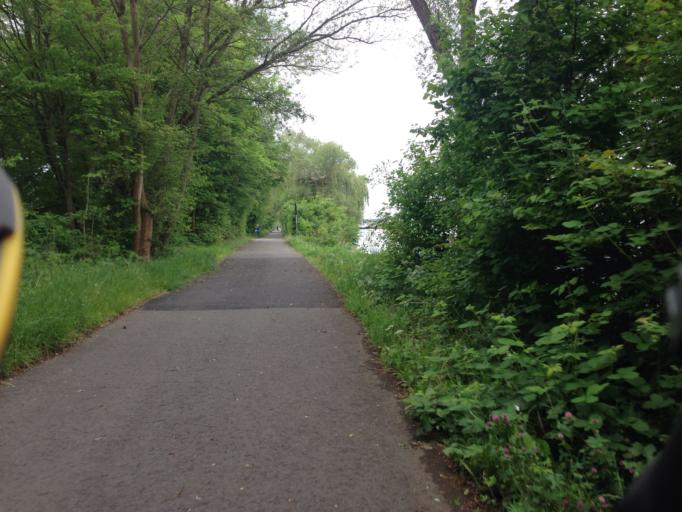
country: DE
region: Hesse
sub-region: Regierungsbezirk Darmstadt
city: Hanau am Main
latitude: 50.1235
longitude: 8.8840
